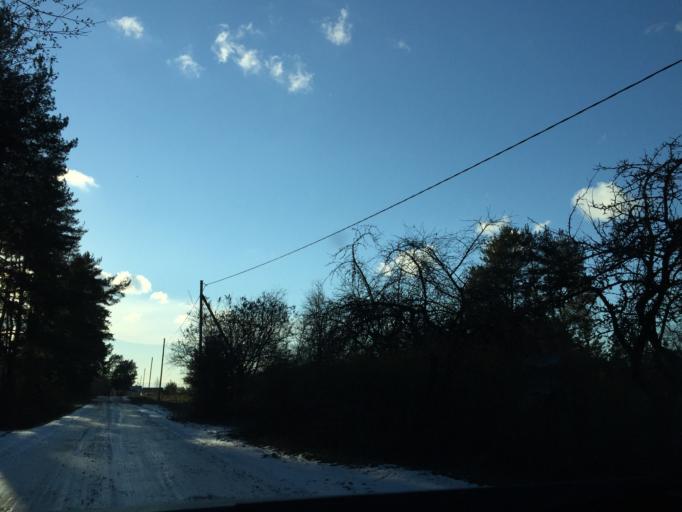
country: LV
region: Kekava
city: Kekava
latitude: 56.8740
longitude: 24.2101
